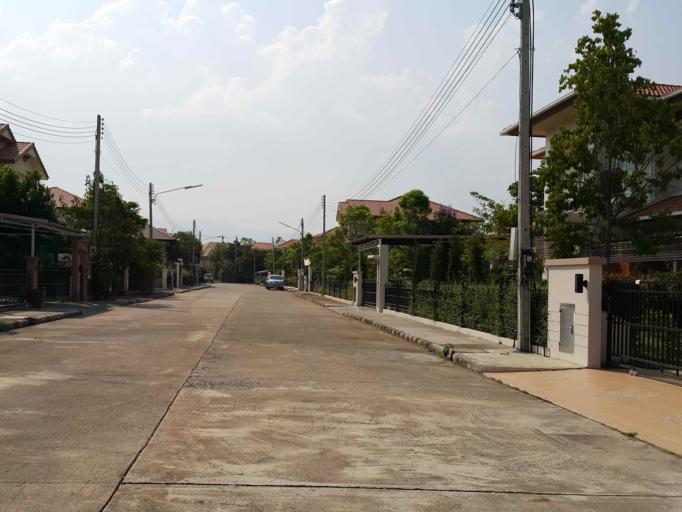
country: TH
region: Chiang Mai
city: Saraphi
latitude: 18.7560
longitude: 99.0433
